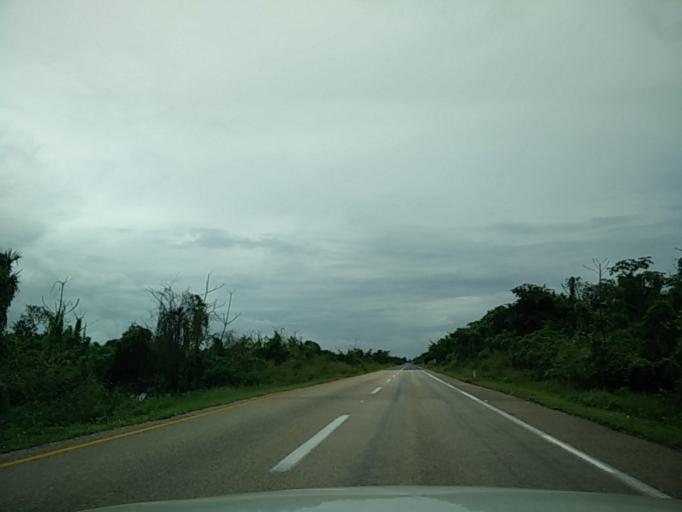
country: MX
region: Quintana Roo
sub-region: Lazaro Cardenas
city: Nuevo Xcan
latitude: 20.8783
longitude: -87.6160
